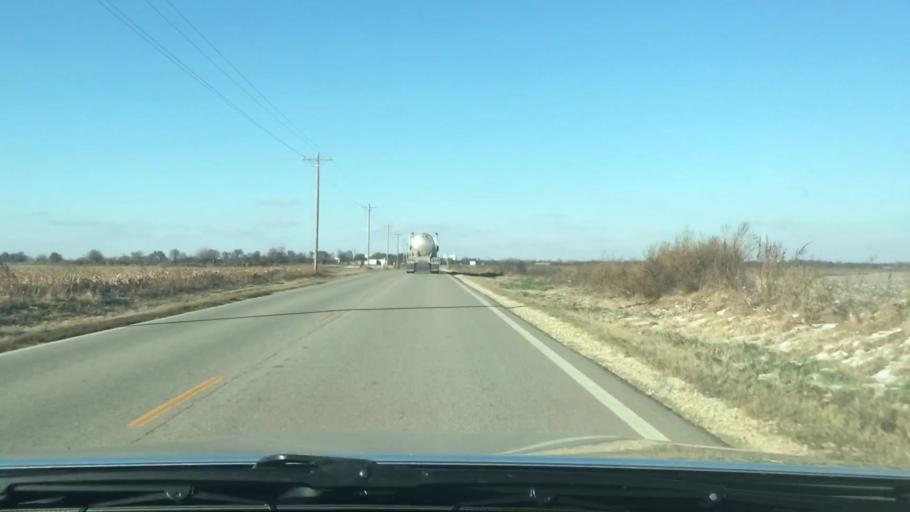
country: US
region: Kansas
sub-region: Rice County
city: Sterling
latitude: 38.1782
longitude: -98.2069
